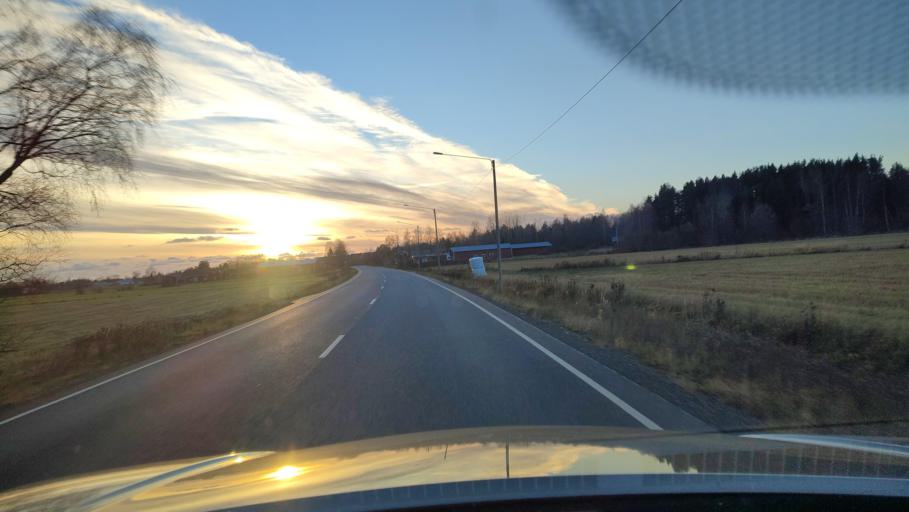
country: FI
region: Southern Ostrobothnia
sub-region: Suupohja
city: Karijoki
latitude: 62.2683
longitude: 21.5547
